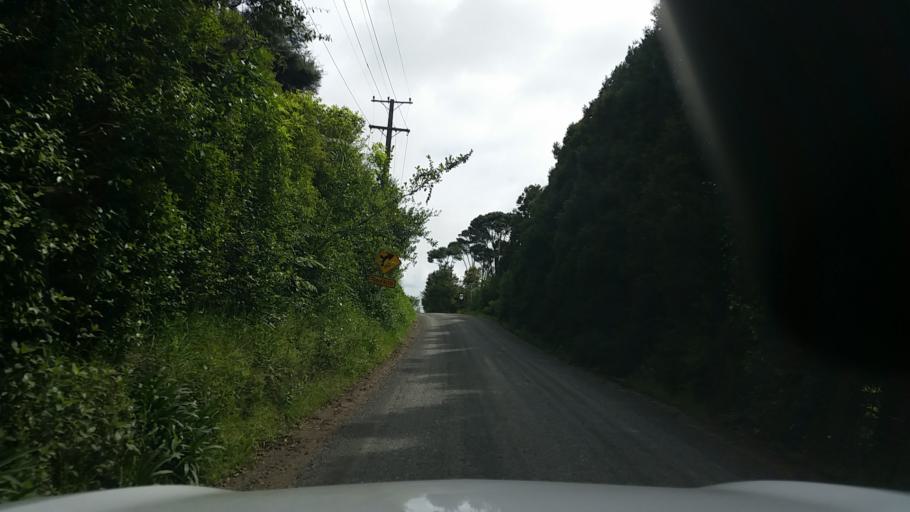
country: NZ
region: Auckland
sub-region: Auckland
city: Muriwai Beach
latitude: -36.8491
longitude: 174.5229
